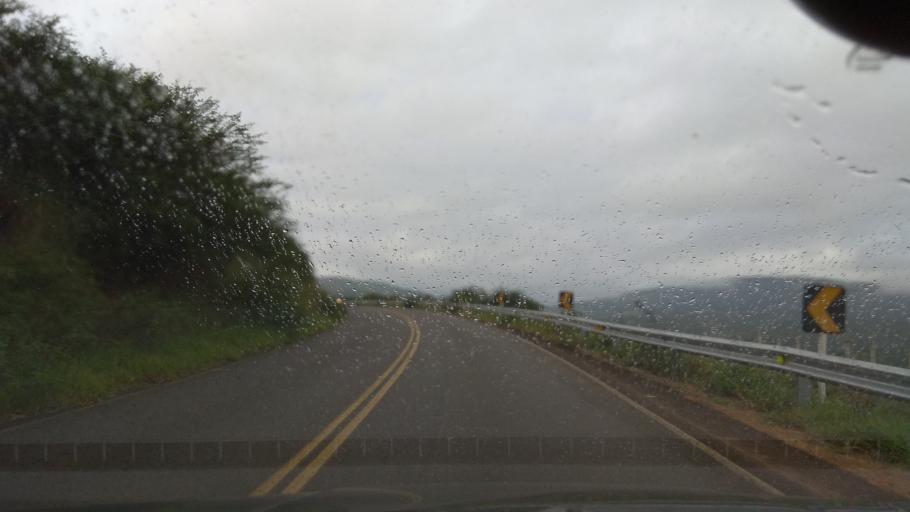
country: BR
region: Bahia
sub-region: Ubaira
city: Ubaira
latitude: -13.2470
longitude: -39.7394
